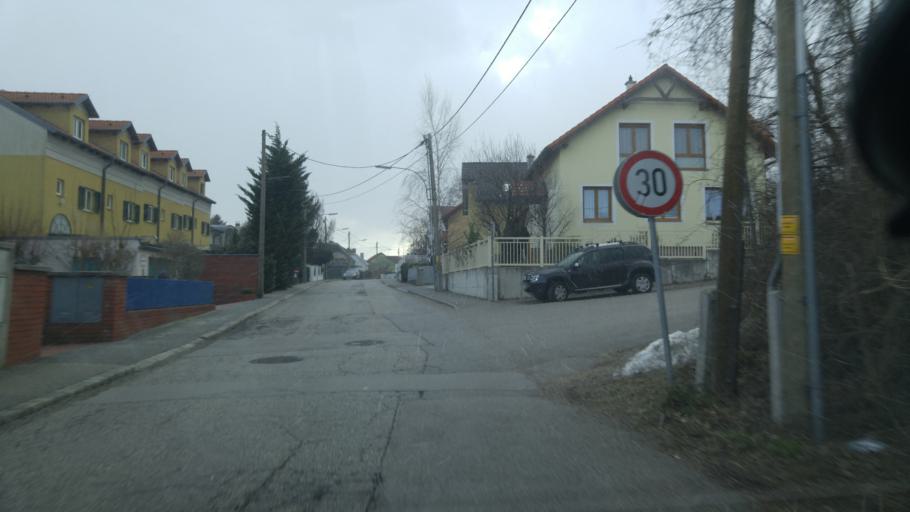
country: AT
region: Lower Austria
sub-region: Politischer Bezirk Baden
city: Baden
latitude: 47.9960
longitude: 16.2101
